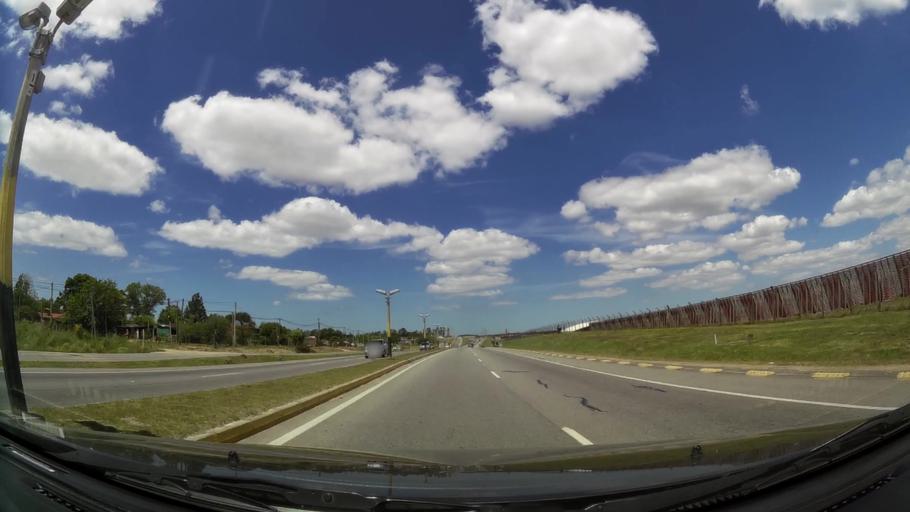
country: UY
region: Canelones
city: Colonia Nicolich
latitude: -34.8258
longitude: -56.0098
